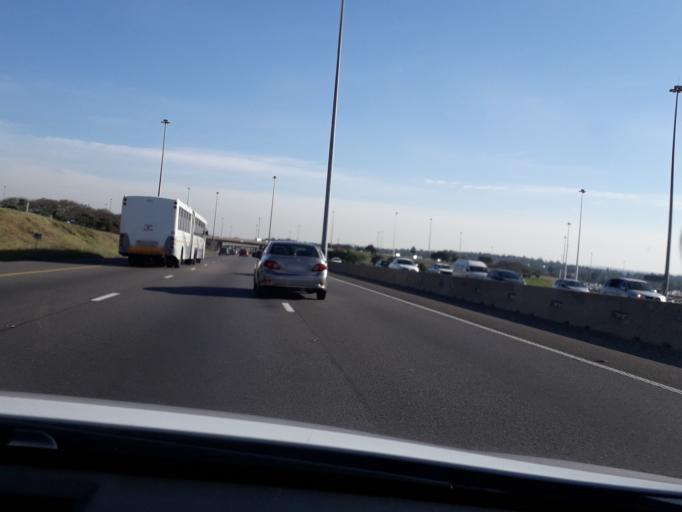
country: ZA
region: Gauteng
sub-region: City of Tshwane Metropolitan Municipality
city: Centurion
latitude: -25.8821
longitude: 28.1676
